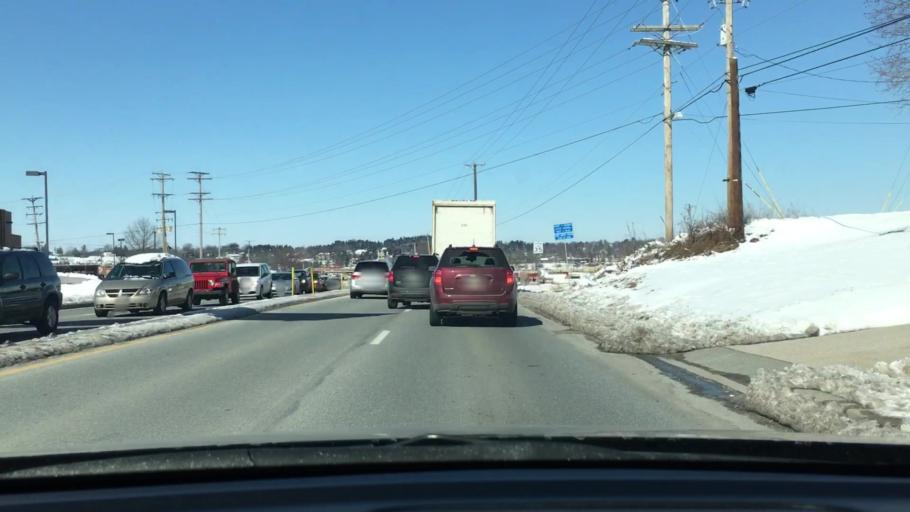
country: US
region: Pennsylvania
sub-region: York County
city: West York
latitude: 39.9629
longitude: -76.7645
